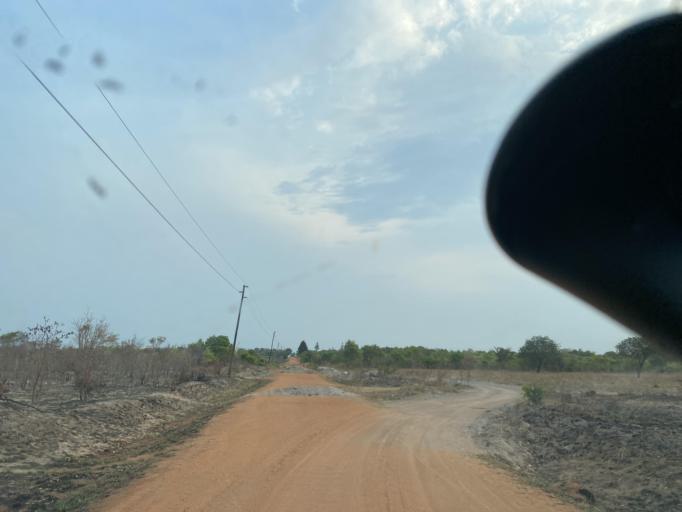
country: ZM
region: Lusaka
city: Chongwe
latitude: -15.2128
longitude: 28.5801
